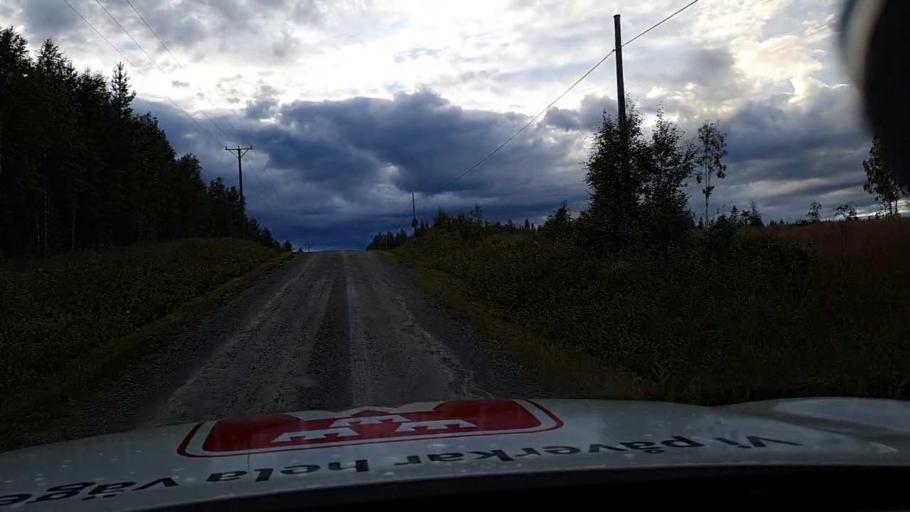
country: SE
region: Jaemtland
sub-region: Bergs Kommun
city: Hoverberg
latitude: 62.8888
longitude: 14.5711
